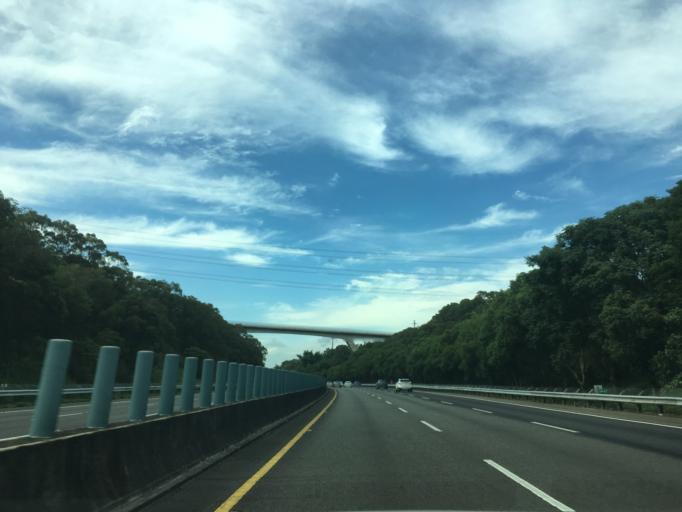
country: TW
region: Taiwan
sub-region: Chiayi
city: Jiayi Shi
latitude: 23.5465
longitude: 120.5034
